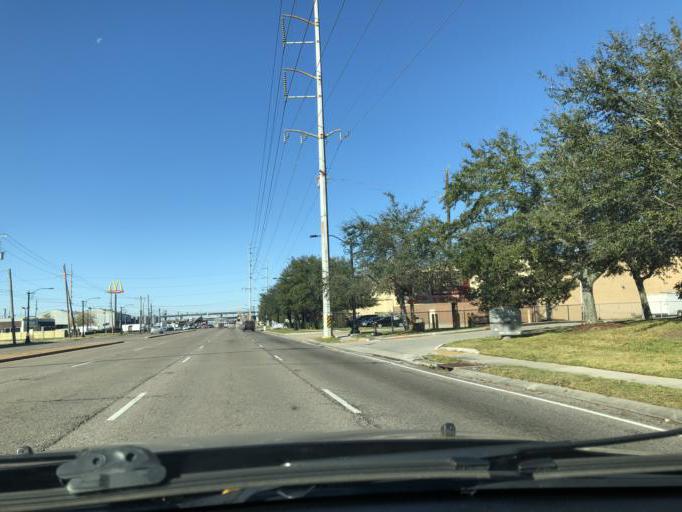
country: US
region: Louisiana
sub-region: Jefferson Parish
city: Jefferson
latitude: 29.9741
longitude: -90.1492
